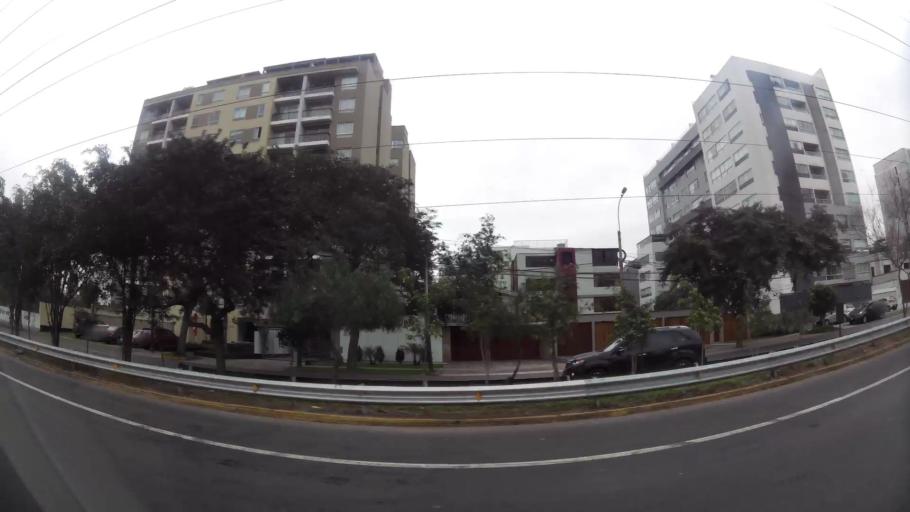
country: PE
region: Lima
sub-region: Lima
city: Surco
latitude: -12.1145
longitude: -76.9778
